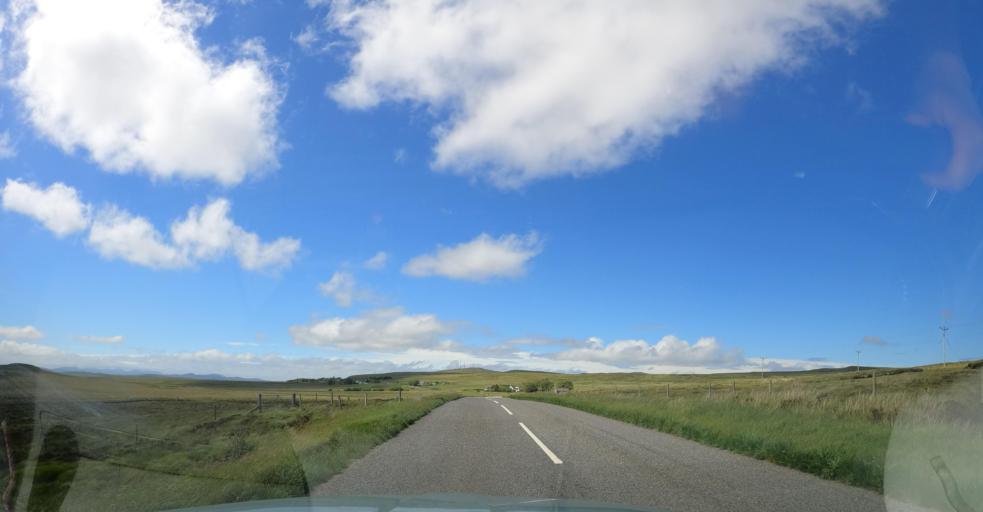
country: GB
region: Scotland
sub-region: Eilean Siar
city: Stornoway
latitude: 58.1621
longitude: -6.5372
